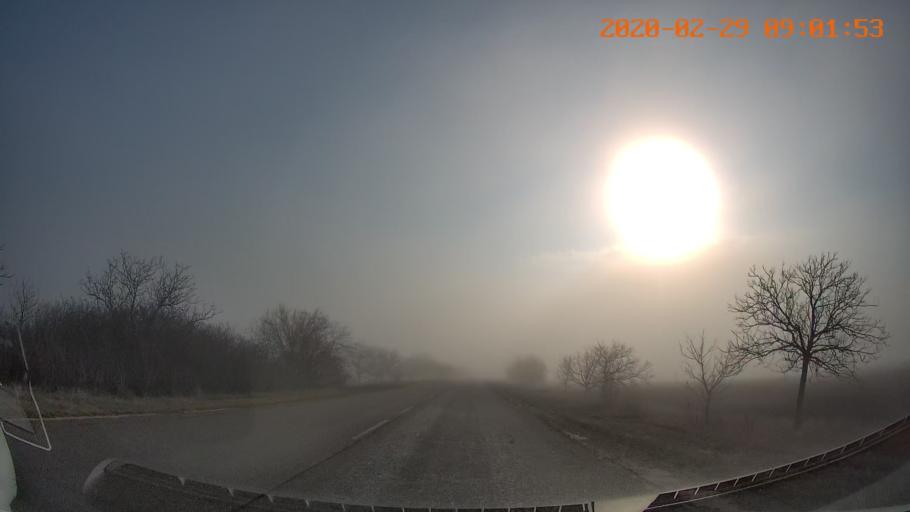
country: UA
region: Odessa
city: Velykoploske
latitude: 46.9233
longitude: 29.7004
